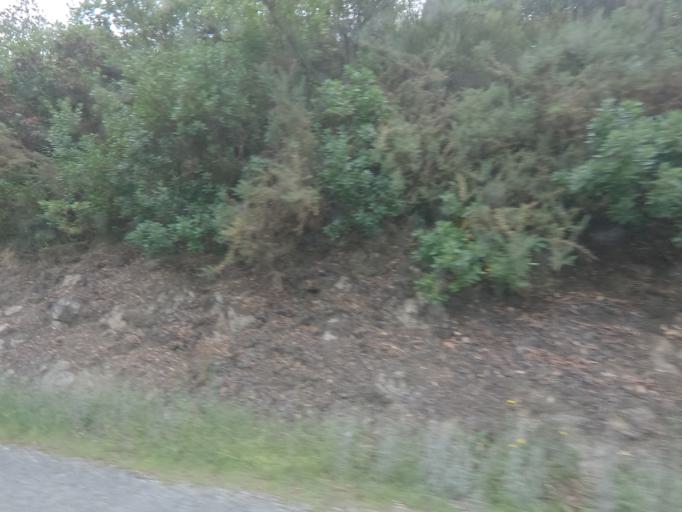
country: PT
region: Viseu
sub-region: Armamar
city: Armamar
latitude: 41.1234
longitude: -7.6558
